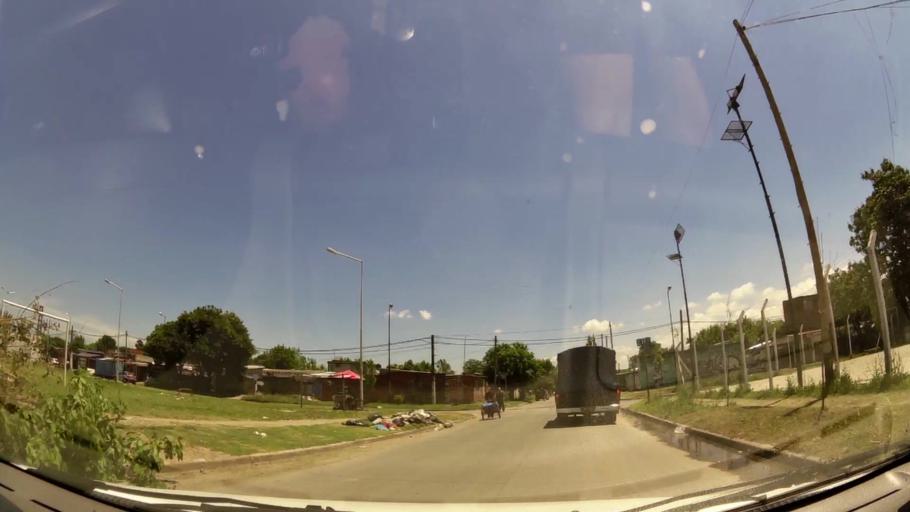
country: AR
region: Buenos Aires
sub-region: Partido de Merlo
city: Merlo
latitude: -34.6490
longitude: -58.7066
